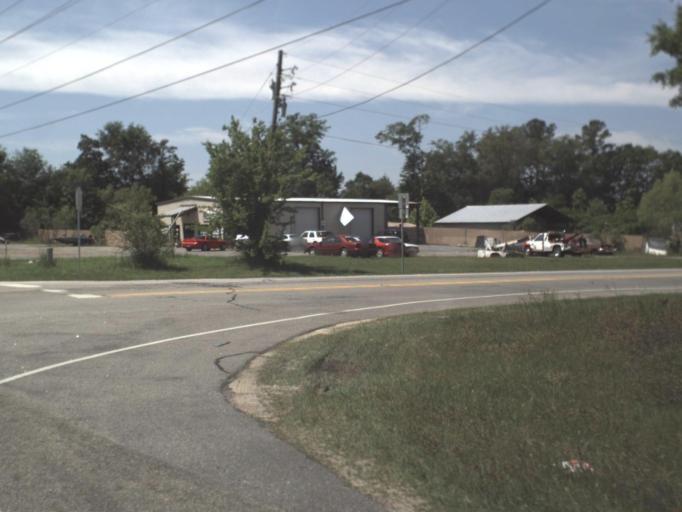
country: US
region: Florida
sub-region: Jackson County
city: Marianna
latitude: 30.7255
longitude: -85.2305
